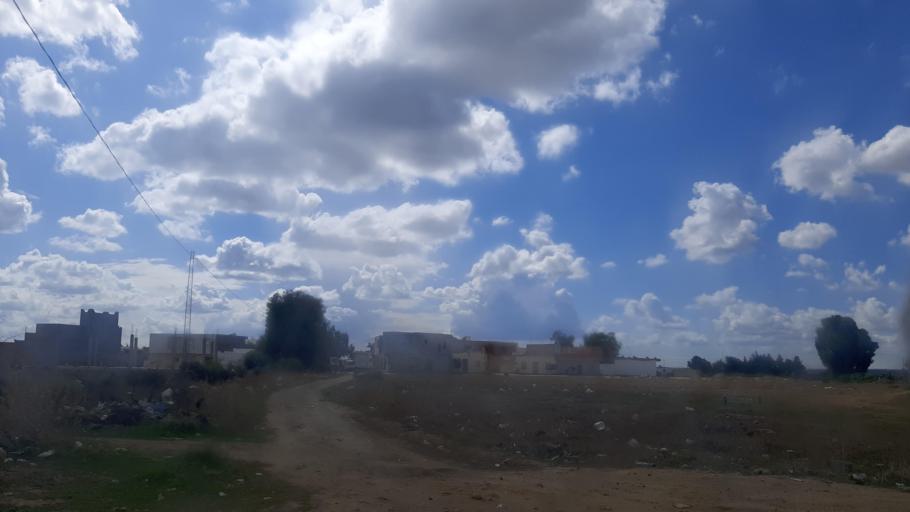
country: TN
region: Nabul
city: Korba
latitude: 36.5926
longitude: 10.8569
